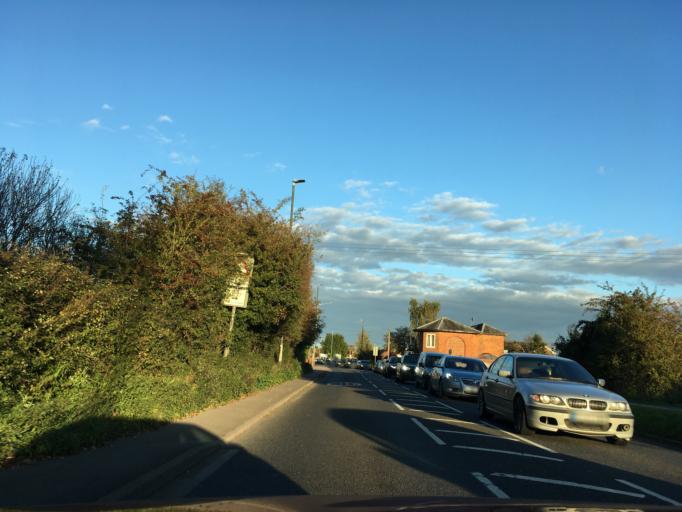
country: GB
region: England
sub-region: Gloucestershire
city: Tewkesbury
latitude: 51.9951
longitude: -2.1432
